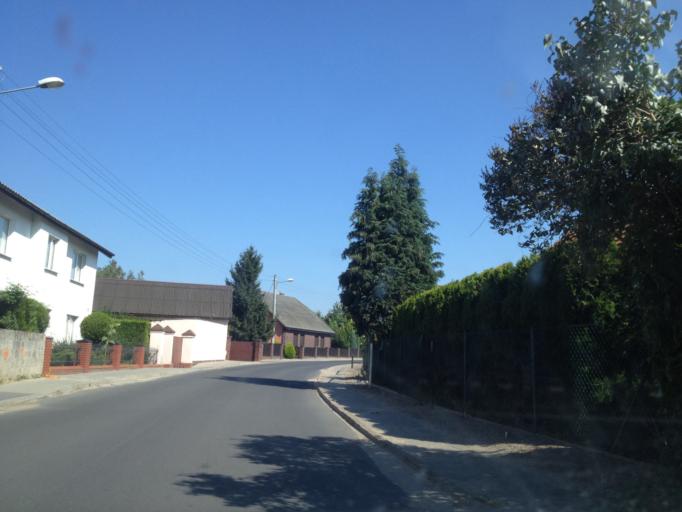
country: PL
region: Greater Poland Voivodeship
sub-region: Powiat sredzki
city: Zaniemysl
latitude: 52.1148
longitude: 17.1162
